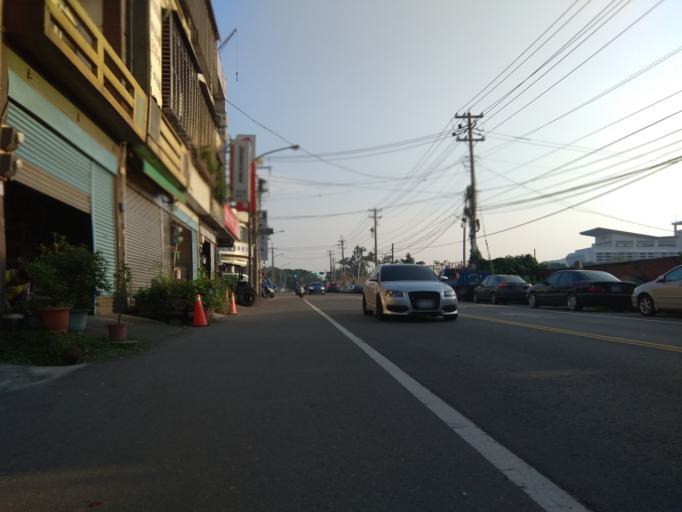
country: TW
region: Taiwan
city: Daxi
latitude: 24.9133
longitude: 121.1873
